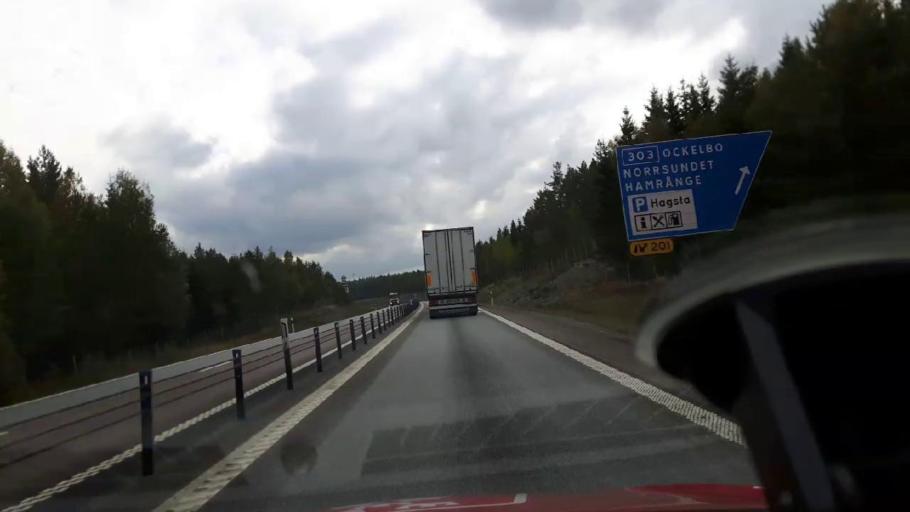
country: SE
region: Gaevleborg
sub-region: Gavle Kommun
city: Norrsundet
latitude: 60.9079
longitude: 17.0148
